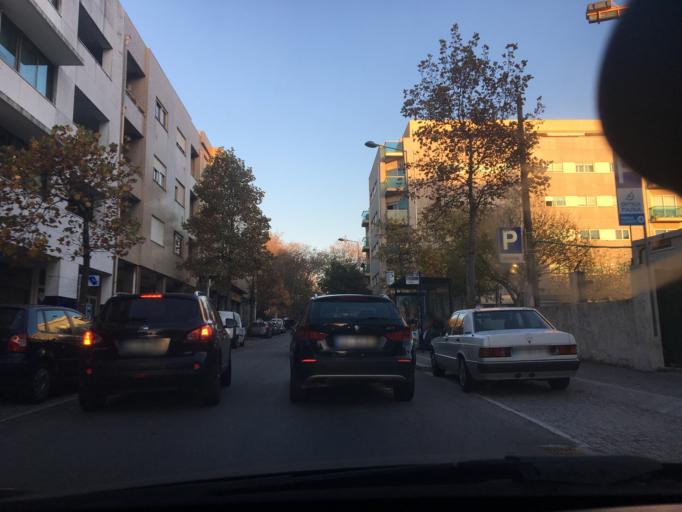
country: PT
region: Porto
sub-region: Matosinhos
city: Matosinhos
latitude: 41.1821
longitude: -8.6854
